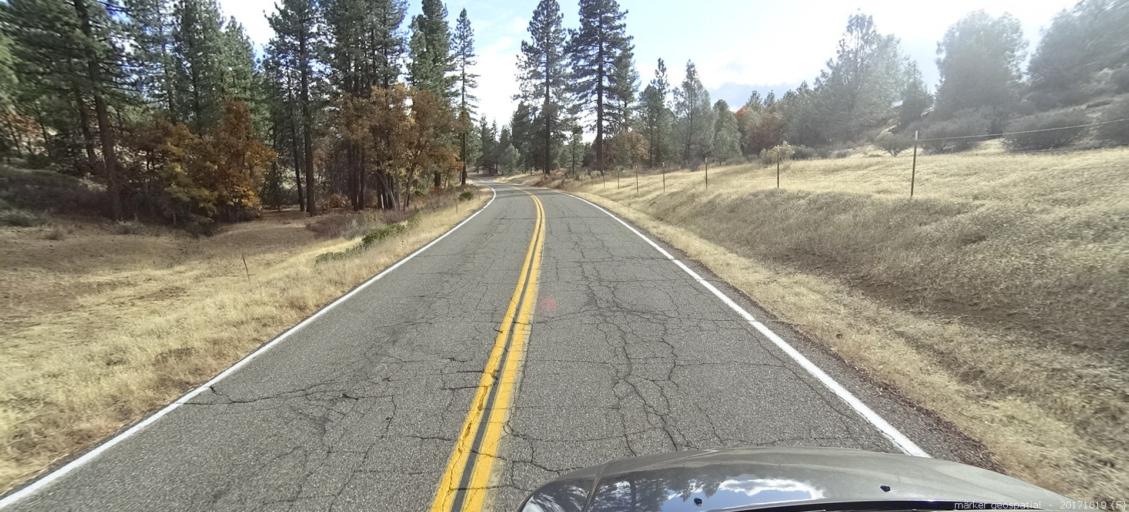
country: US
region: California
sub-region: Shasta County
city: Burney
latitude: 40.9488
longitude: -121.4411
